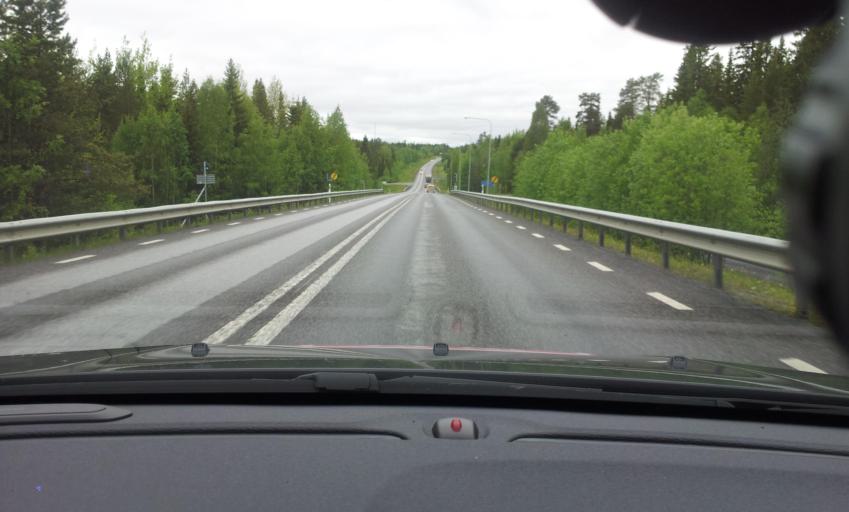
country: SE
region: Jaemtland
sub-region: Krokoms Kommun
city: Valla
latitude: 63.3061
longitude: 13.8343
